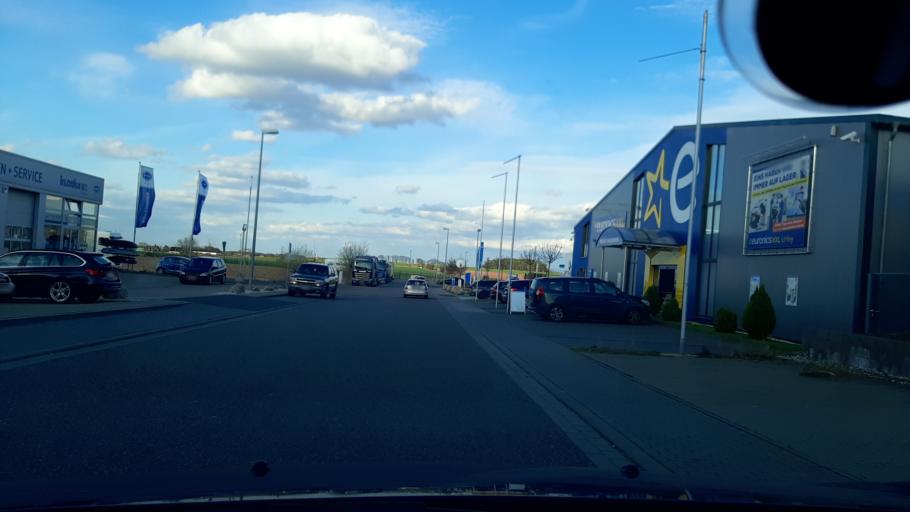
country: DE
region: North Rhine-Westphalia
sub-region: Regierungsbezirk Koln
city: Mechernich
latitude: 50.6186
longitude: 6.6497
